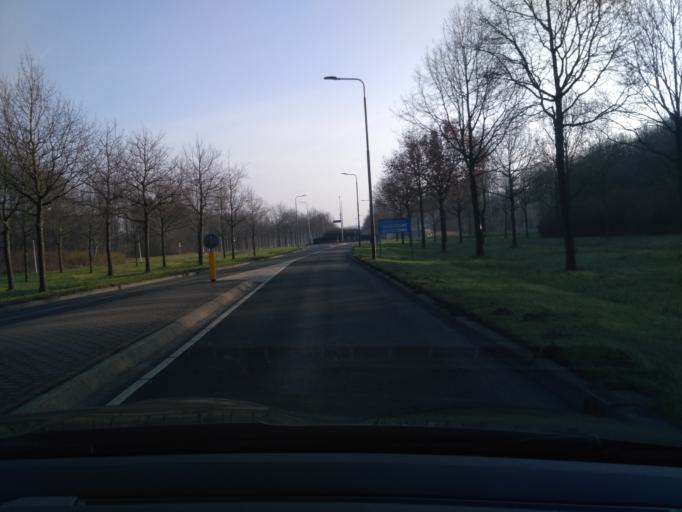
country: NL
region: Flevoland
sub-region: Gemeente Dronten
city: Dronten
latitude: 52.5210
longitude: 5.6956
